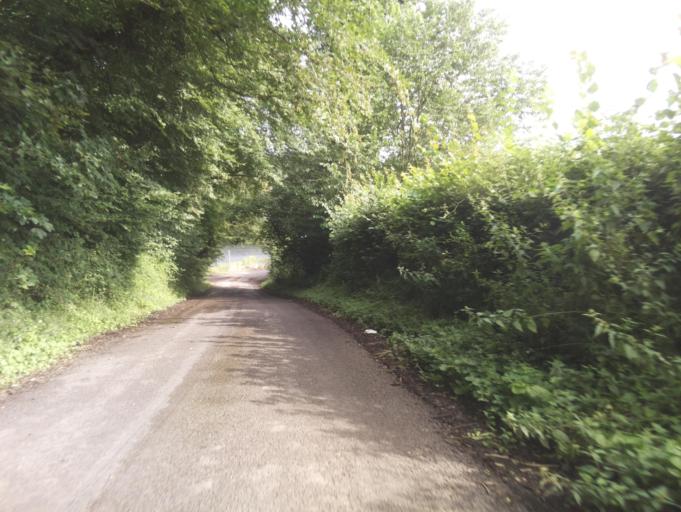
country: GB
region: England
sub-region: Somerset
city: Chilcompton
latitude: 51.2556
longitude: -2.5521
